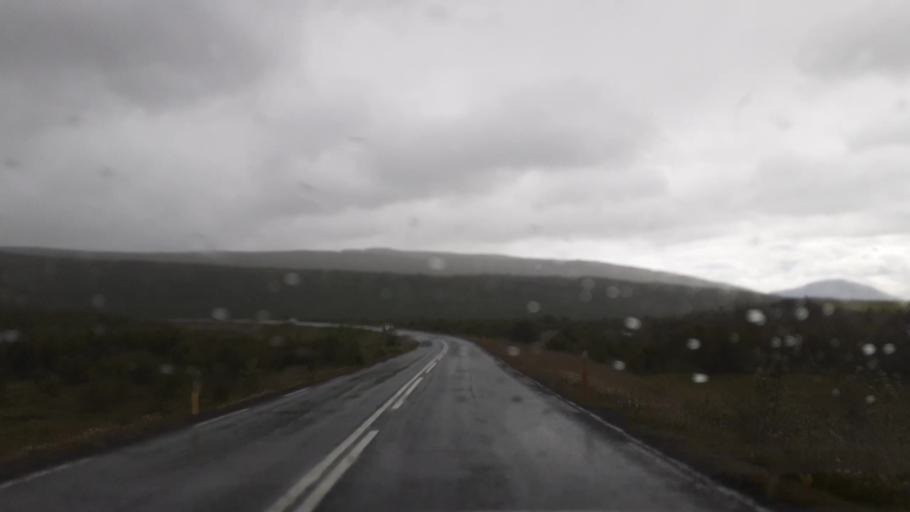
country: IS
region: East
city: Egilsstadir
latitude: 65.2685
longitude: -14.3468
